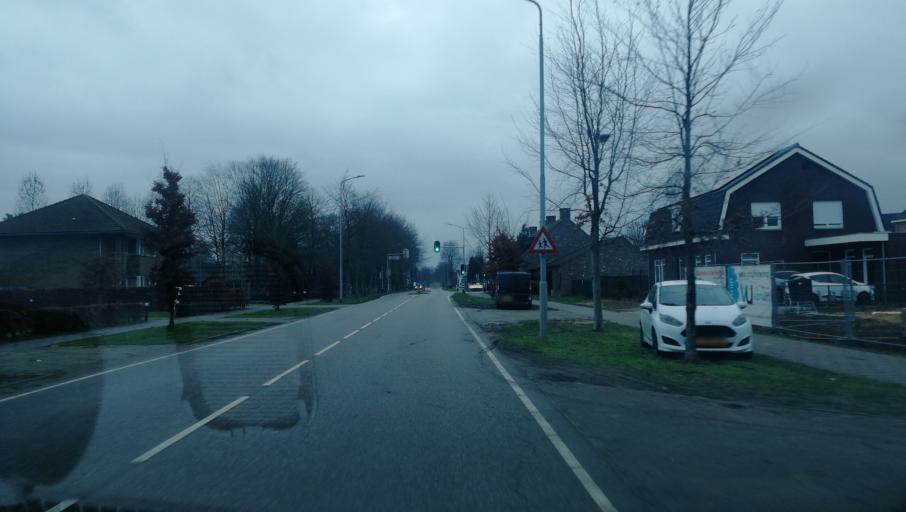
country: NL
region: Limburg
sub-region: Gemeente Venlo
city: Tegelen
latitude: 51.3579
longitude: 6.1345
